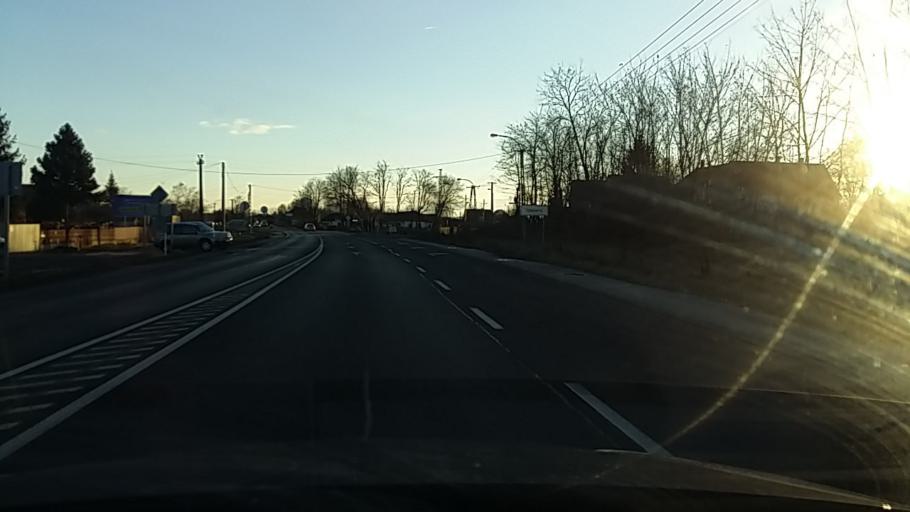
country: HU
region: Szabolcs-Szatmar-Bereg
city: Ujfeherto
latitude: 47.8252
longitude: 21.6989
